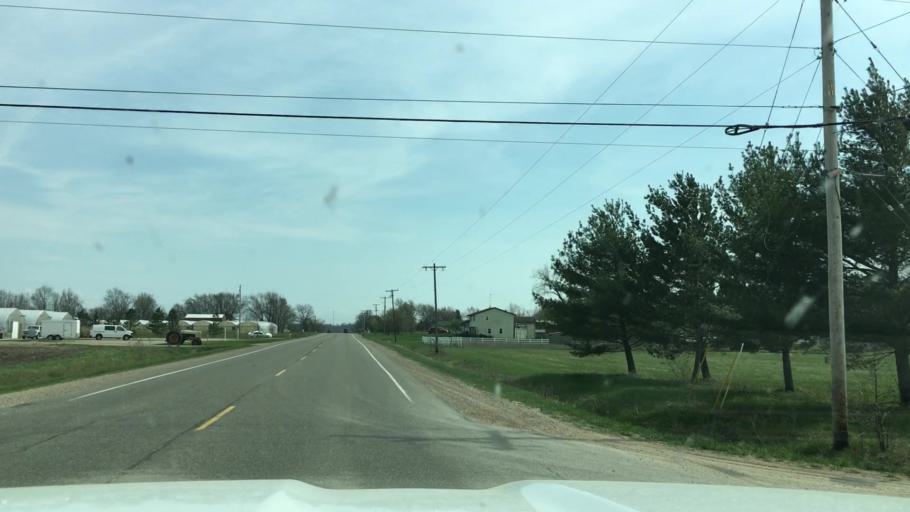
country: US
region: Michigan
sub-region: Ottawa County
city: Hudsonville
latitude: 42.8706
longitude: -85.9011
